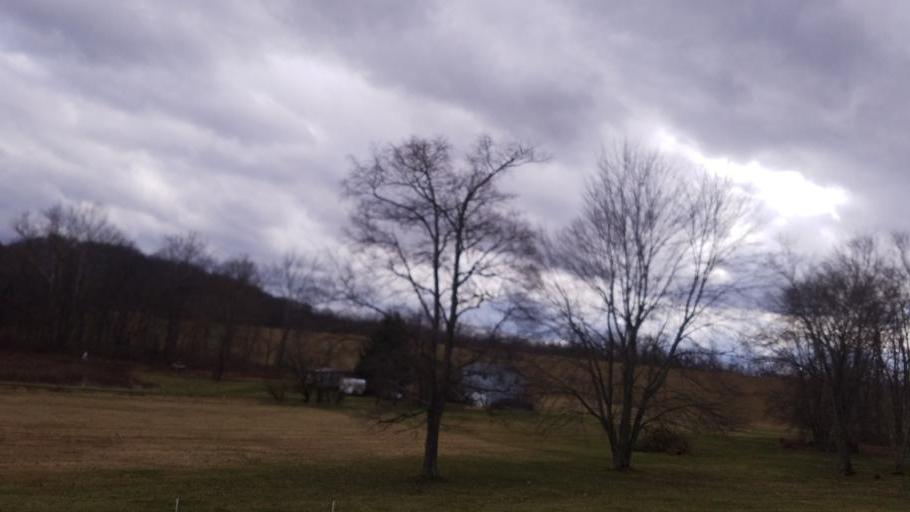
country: US
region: Ohio
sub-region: Muskingum County
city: Frazeysburg
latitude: 40.0768
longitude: -82.1587
